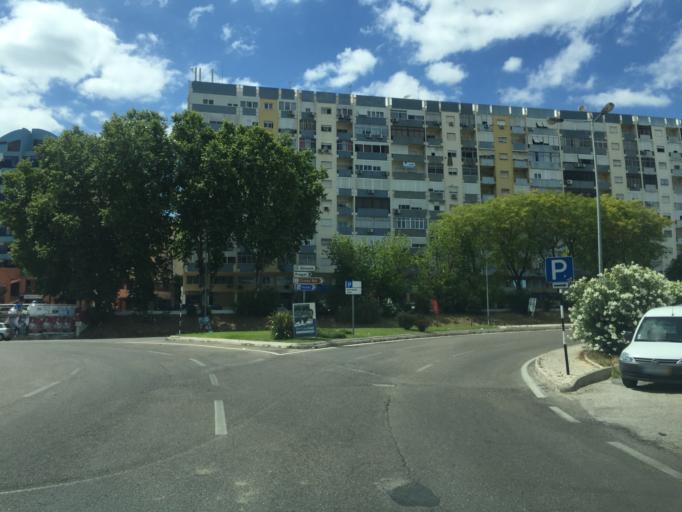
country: PT
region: Setubal
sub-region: Almada
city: Pragal
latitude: 38.6671
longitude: -9.1662
